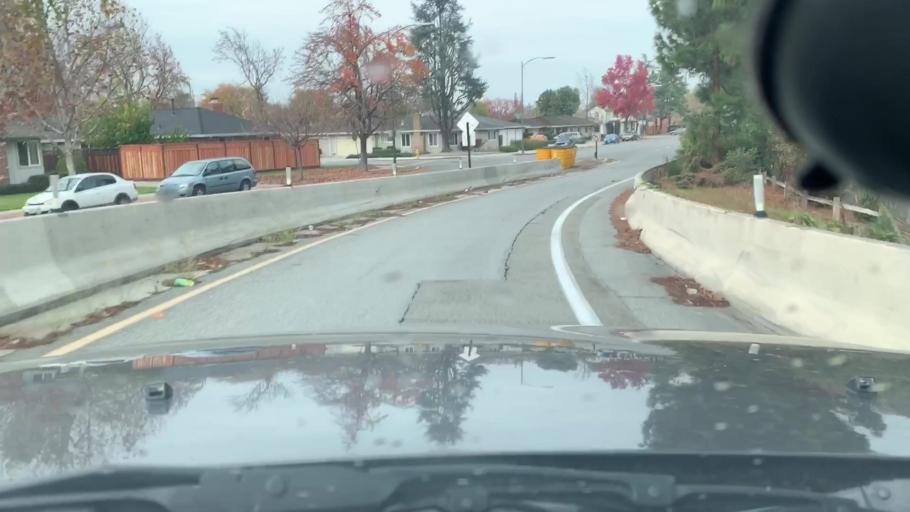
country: US
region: California
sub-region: Santa Clara County
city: Seven Trees
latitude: 37.2859
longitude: -121.8849
